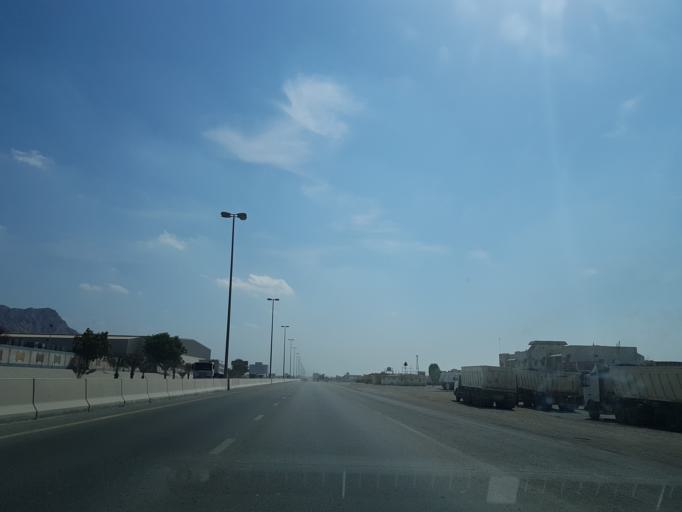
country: AE
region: Ra's al Khaymah
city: Ras al-Khaimah
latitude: 25.8570
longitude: 56.0207
